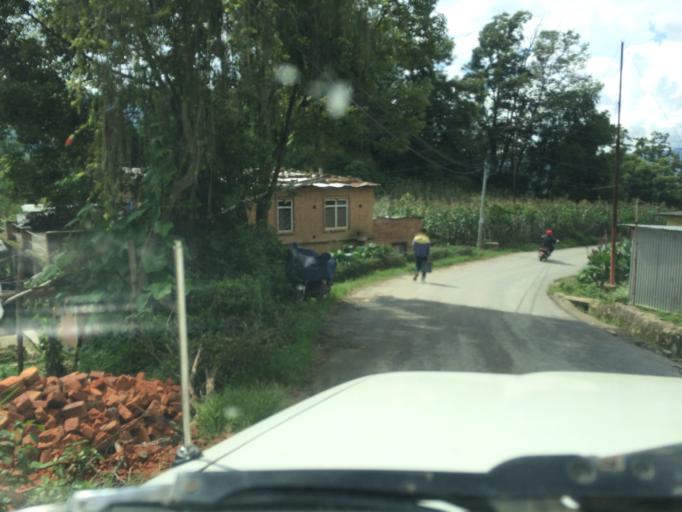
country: NP
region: Central Region
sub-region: Bagmati Zone
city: Patan
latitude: 27.6098
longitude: 85.3077
